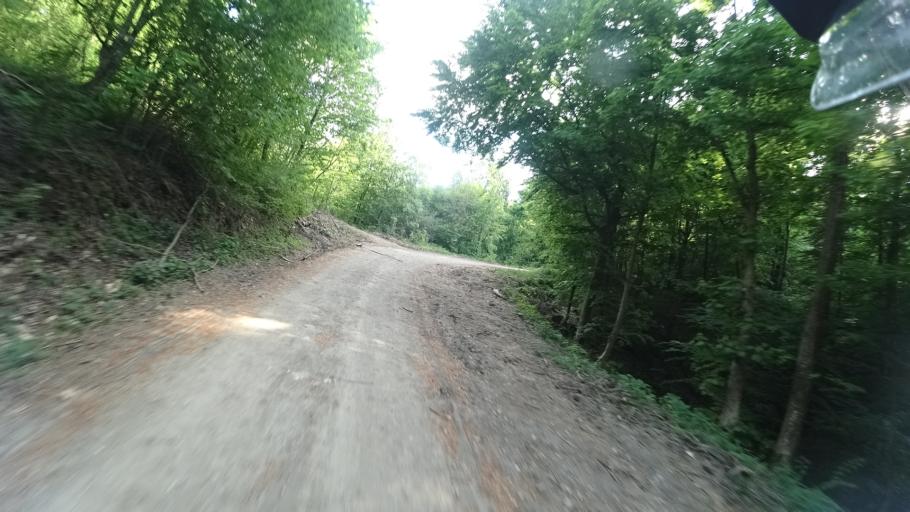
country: HR
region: Zagrebacka
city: Jablanovec
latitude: 45.8538
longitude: 15.8909
